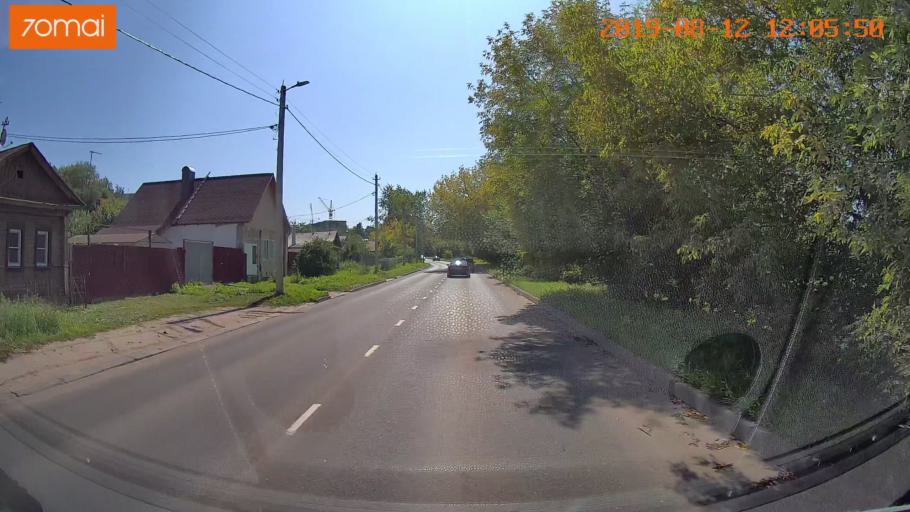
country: RU
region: Ivanovo
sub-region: Gorod Ivanovo
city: Ivanovo
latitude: 56.9921
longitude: 41.0188
